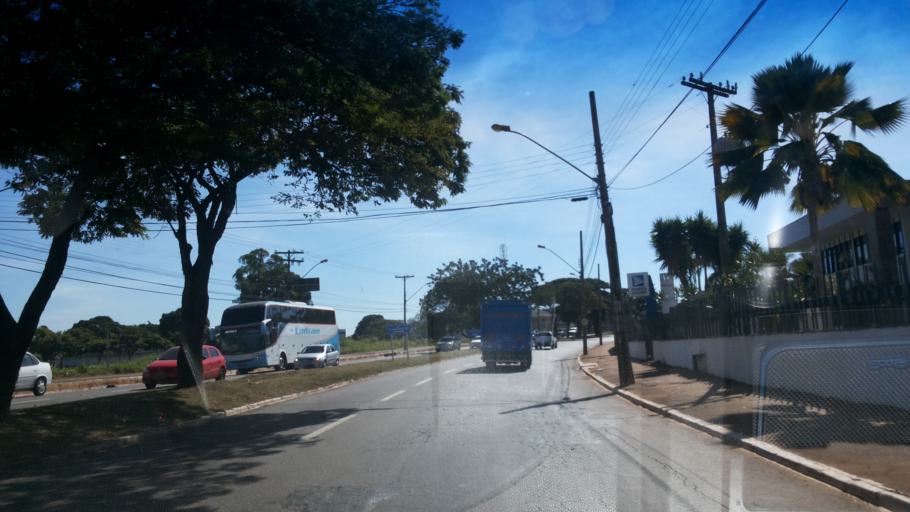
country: BR
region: Goias
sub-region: Goiania
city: Goiania
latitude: -16.6437
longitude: -49.2422
